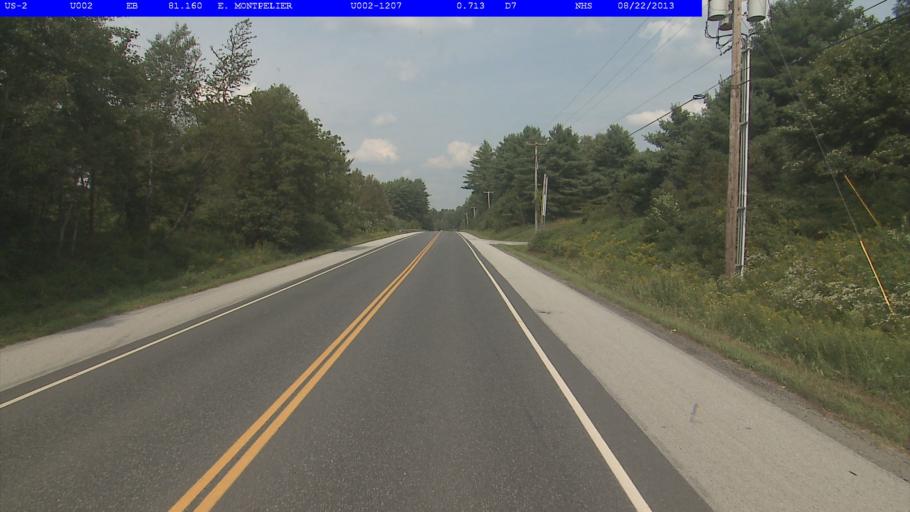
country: US
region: Vermont
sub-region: Washington County
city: Barre
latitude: 44.2442
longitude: -72.5046
